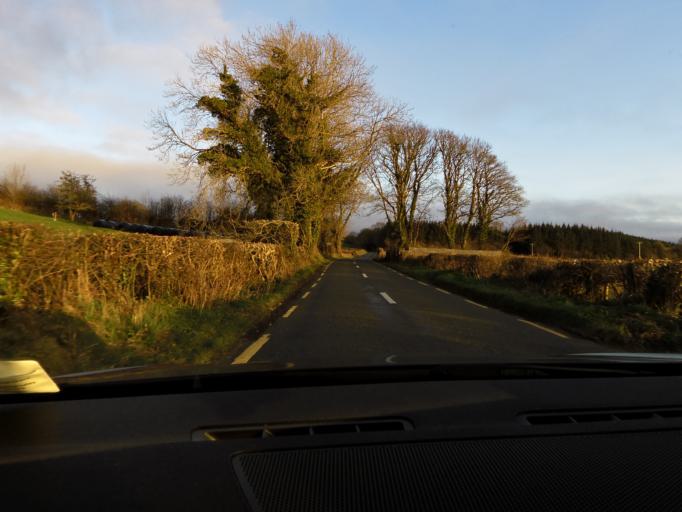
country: IE
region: Connaught
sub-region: Sligo
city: Tobercurry
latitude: 54.0410
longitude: -8.6227
